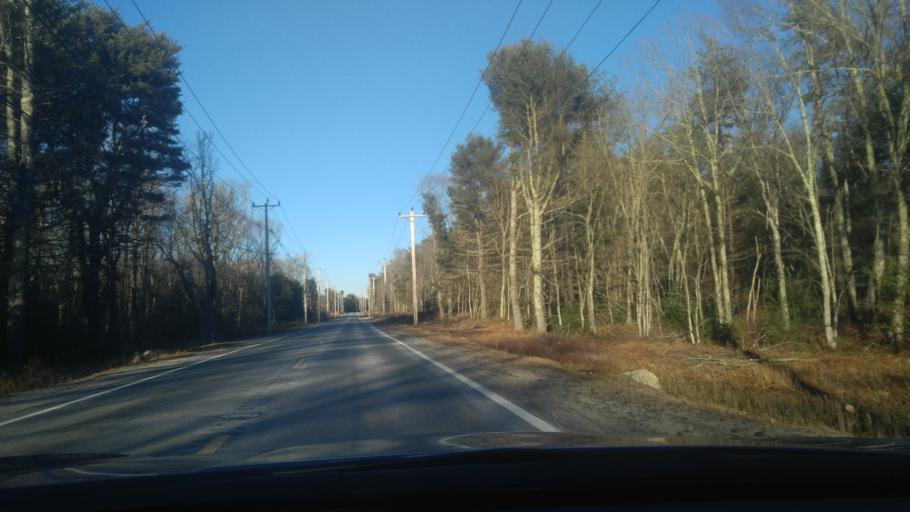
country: US
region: Rhode Island
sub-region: Kent County
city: West Warwick
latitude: 41.6516
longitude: -71.5674
